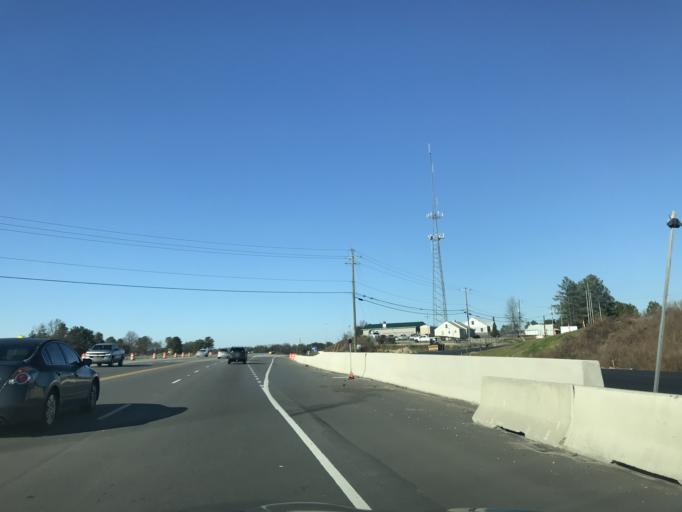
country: US
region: North Carolina
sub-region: Durham County
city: Durham
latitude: 35.9867
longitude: -78.8609
